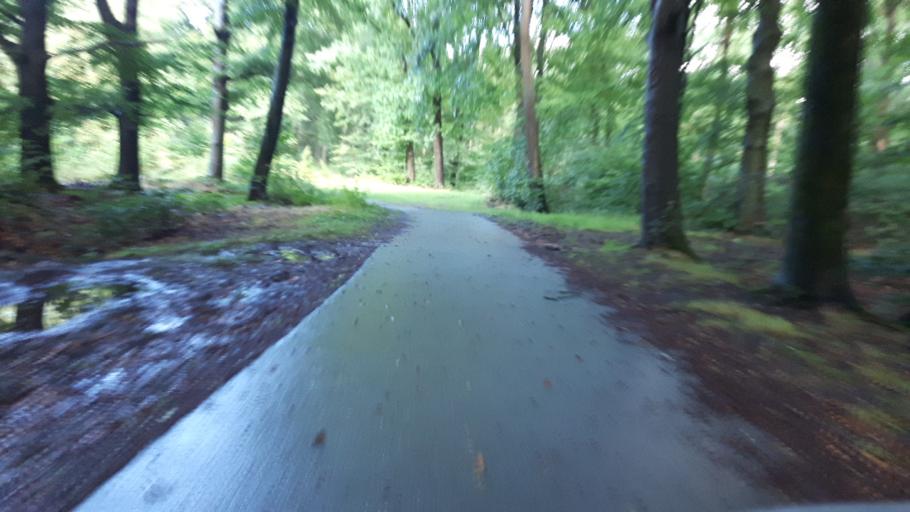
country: NL
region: Friesland
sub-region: Gemeente Smallingerland
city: Drachten
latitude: 53.0654
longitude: 6.1213
